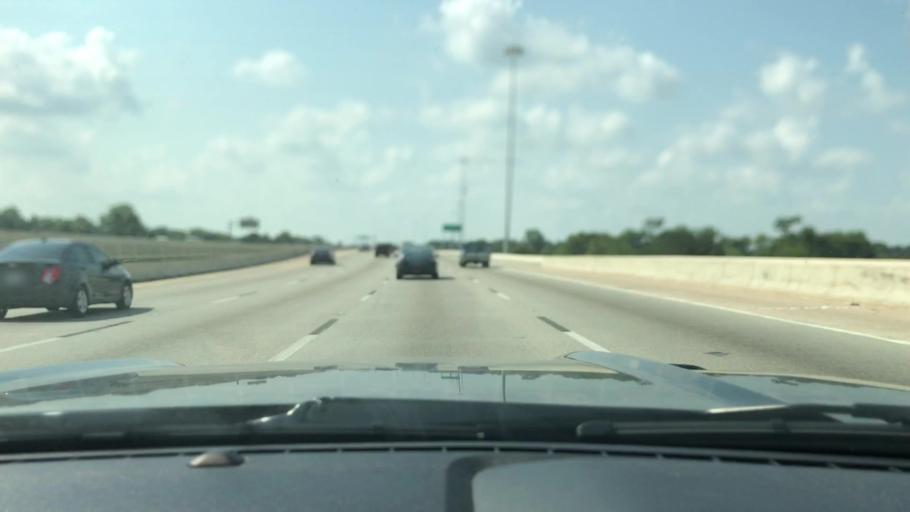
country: US
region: Texas
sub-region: Harris County
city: Aldine
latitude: 29.8625
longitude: -95.3335
